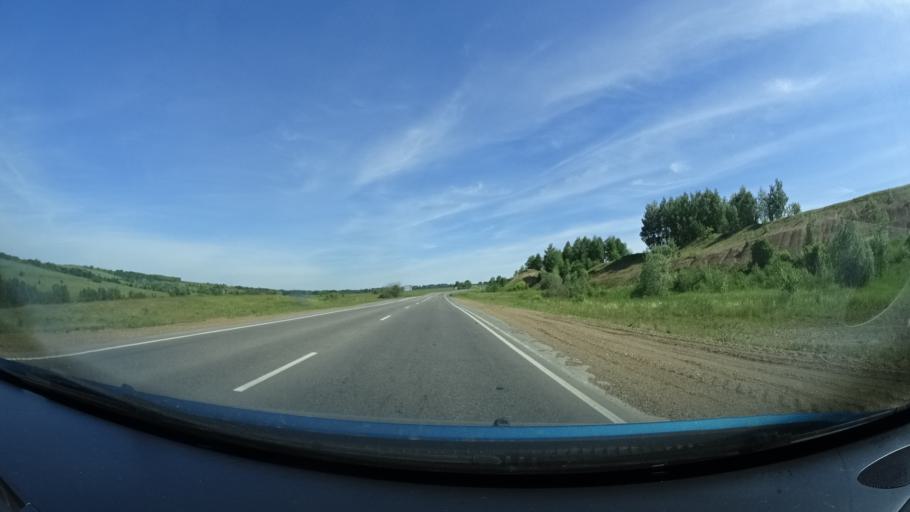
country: RU
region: Bashkortostan
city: Blagoveshchensk
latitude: 55.1175
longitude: 55.8408
